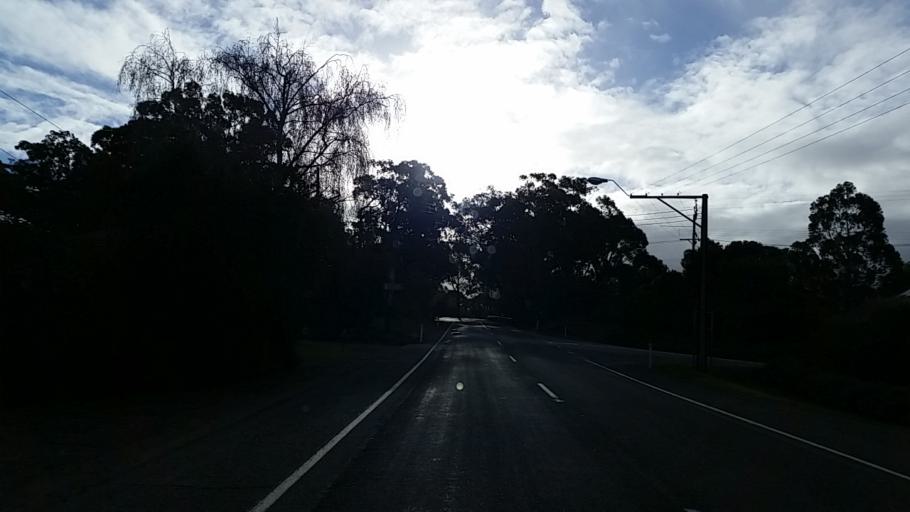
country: AU
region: South Australia
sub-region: Adelaide Hills
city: Bridgewater
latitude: -34.9643
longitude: 138.7673
